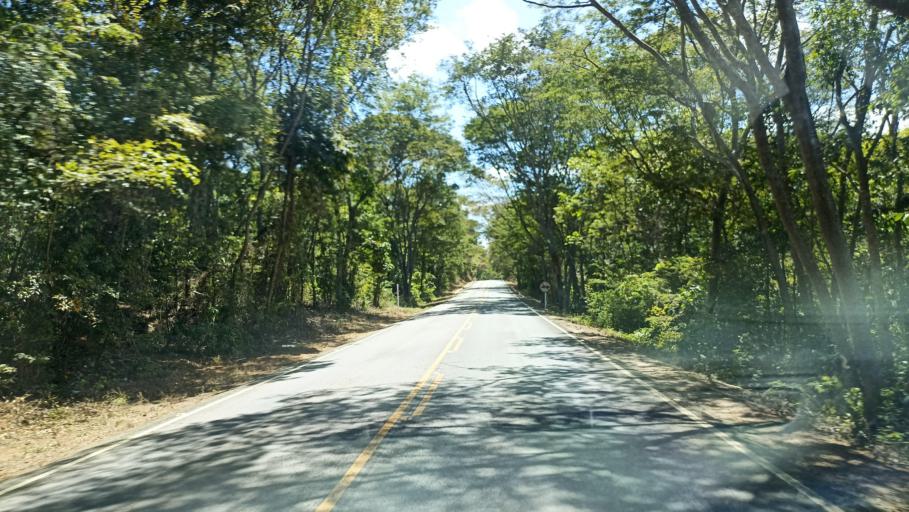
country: BR
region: Bahia
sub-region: Andarai
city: Vera Cruz
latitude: -12.7740
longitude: -41.3303
